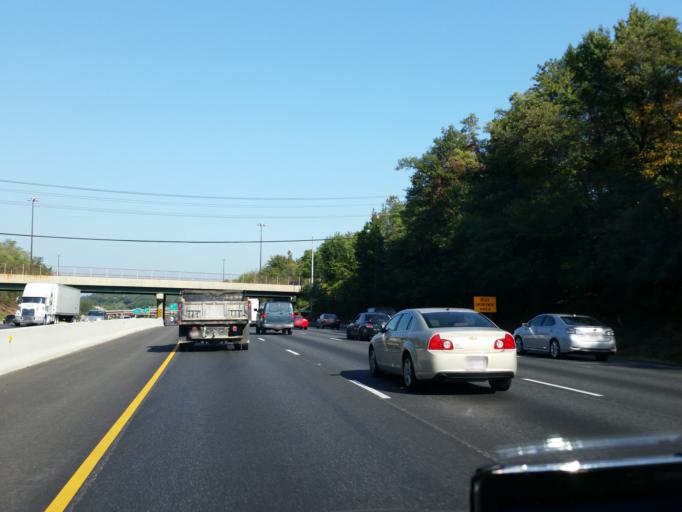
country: US
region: Maryland
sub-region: Prince George's County
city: Glenarden
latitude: 38.9382
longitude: -76.8555
